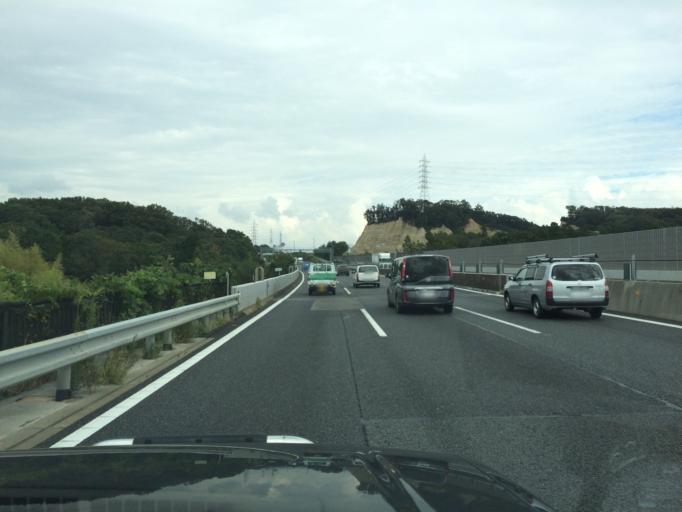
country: JP
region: Mie
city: Yokkaichi
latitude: 35.0100
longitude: 136.5835
